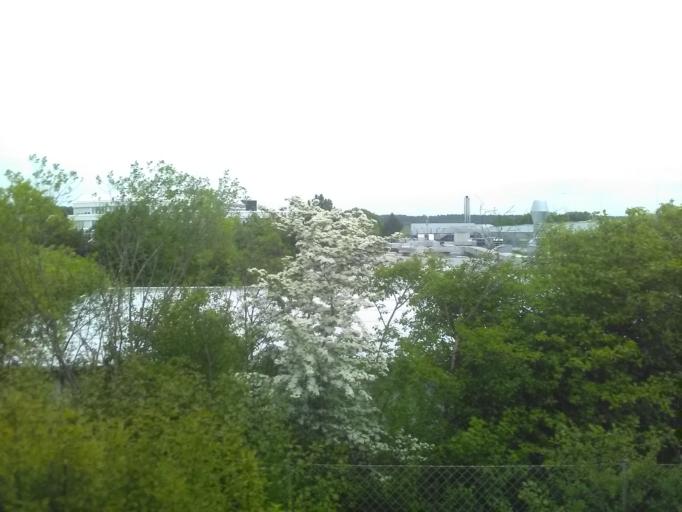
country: DE
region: Bavaria
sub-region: Regierungsbezirk Mittelfranken
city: Heroldsberg
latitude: 49.5447
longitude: 11.1468
